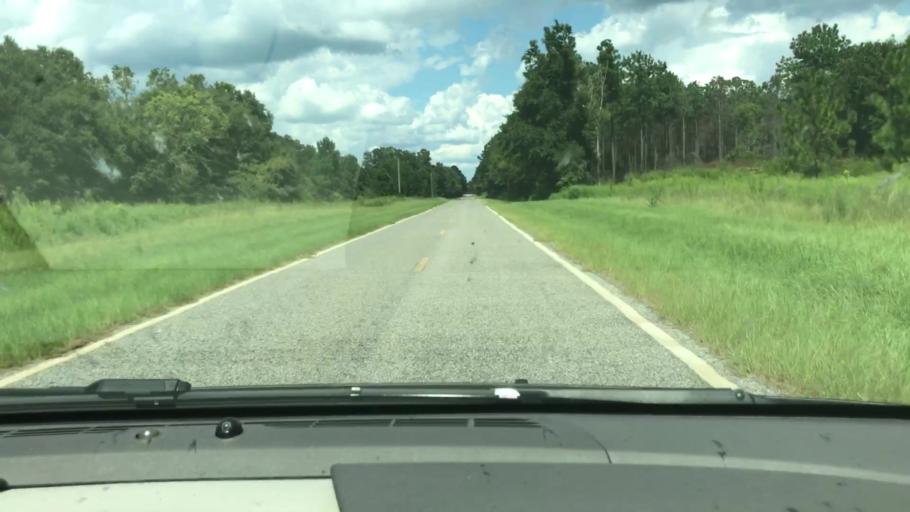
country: US
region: Georgia
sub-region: Clay County
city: Fort Gaines
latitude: 31.7409
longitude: -85.0857
